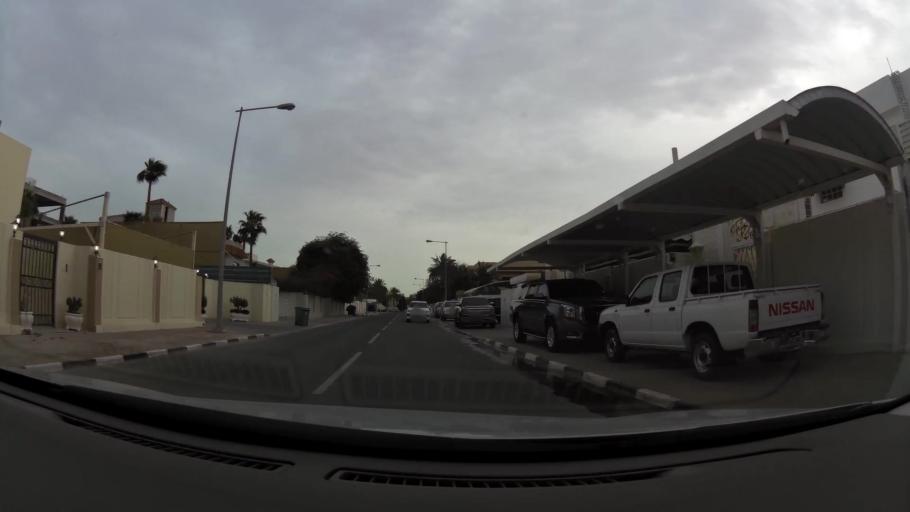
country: QA
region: Baladiyat ad Dawhah
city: Doha
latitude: 25.3337
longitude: 51.5067
